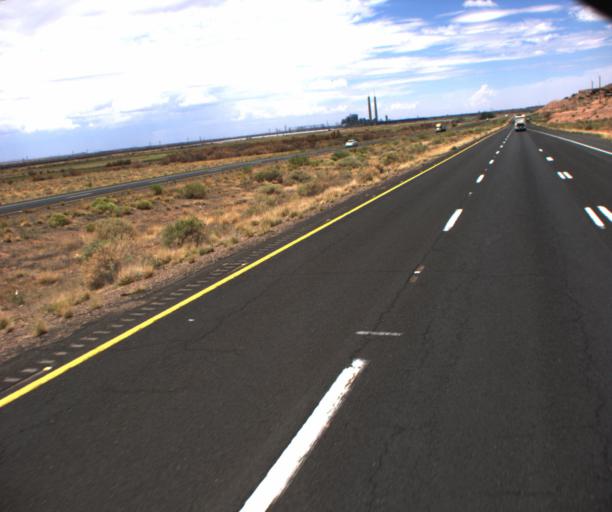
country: US
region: Arizona
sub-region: Navajo County
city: Joseph City
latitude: 34.9255
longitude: -110.2641
